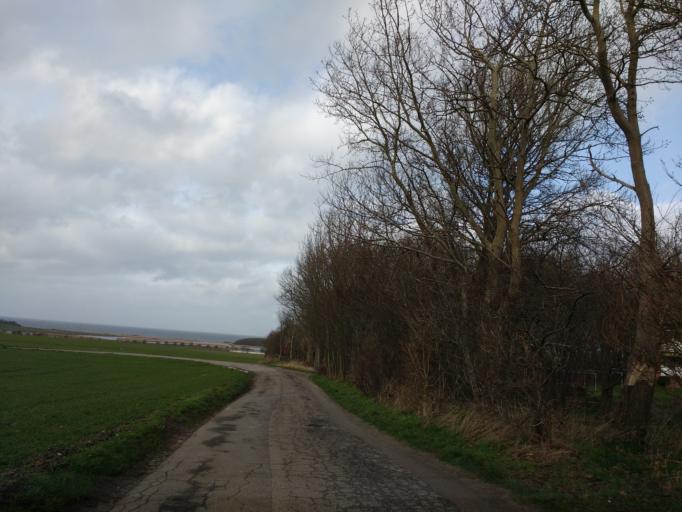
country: DE
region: Schleswig-Holstein
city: Heiligenhafen
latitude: 54.3711
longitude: 10.9501
